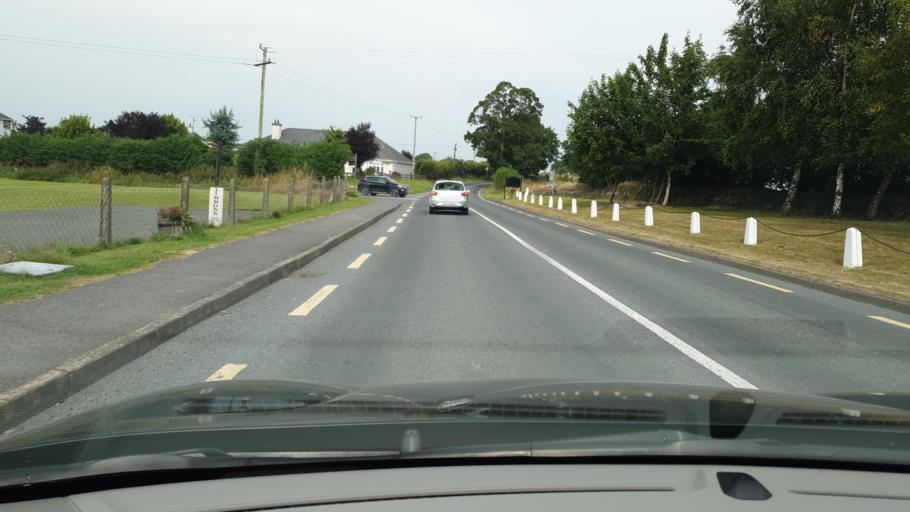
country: IE
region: Leinster
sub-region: An Mhi
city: Athboy
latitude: 53.6701
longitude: -6.9024
